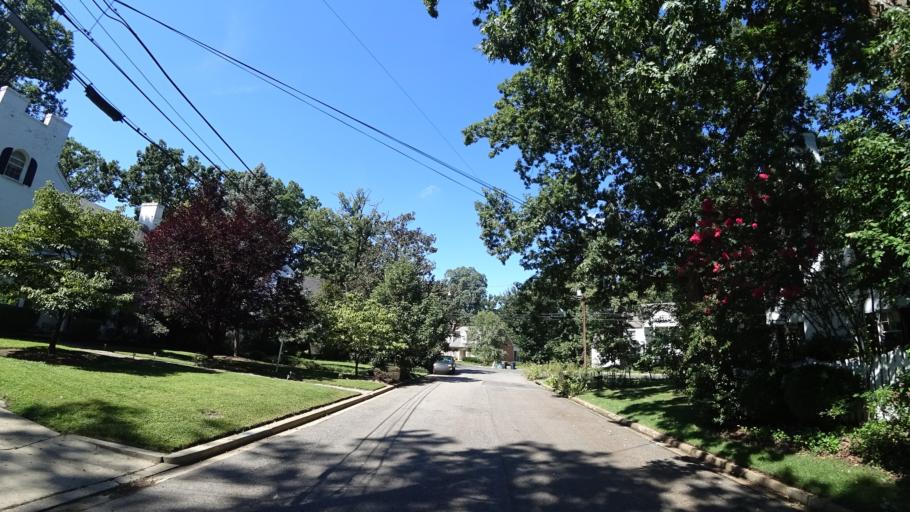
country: US
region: Washington, D.C.
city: Washington, D.C.
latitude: 38.9389
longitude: -77.0435
